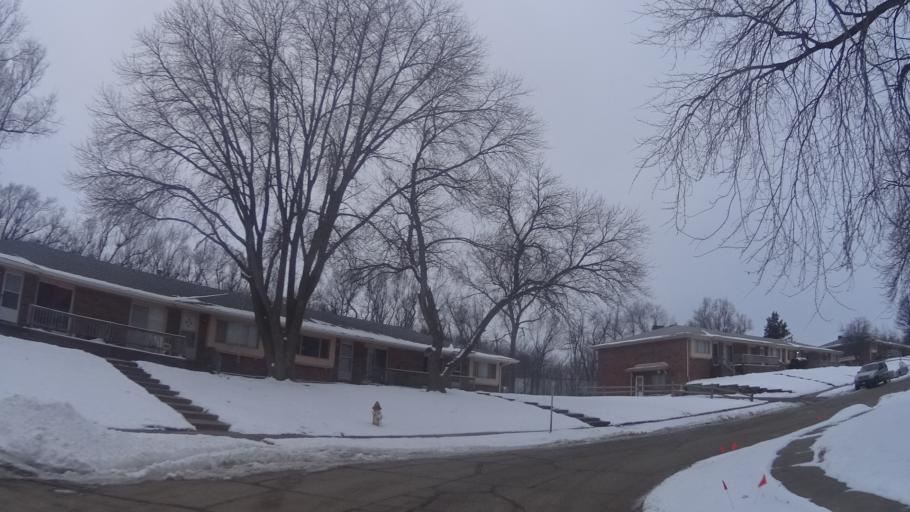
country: US
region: Nebraska
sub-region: Sarpy County
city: Offutt Air Force Base
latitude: 41.1414
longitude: -95.9245
